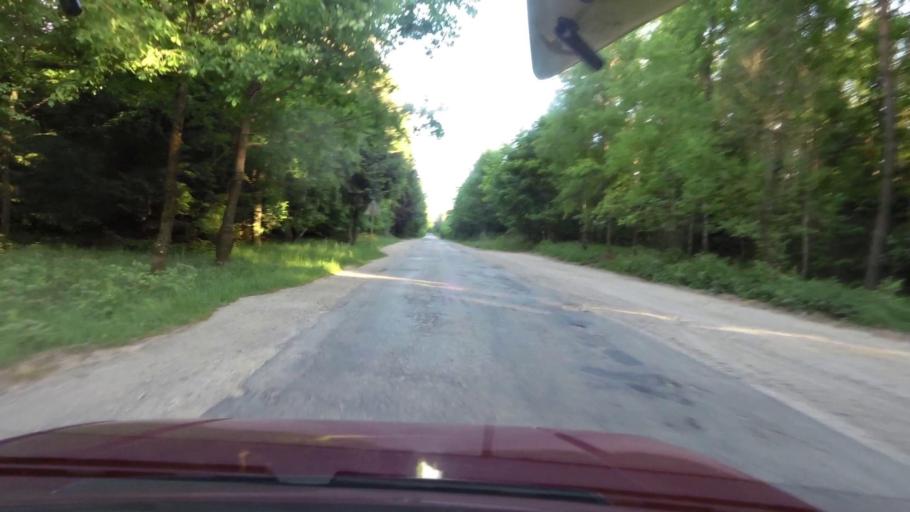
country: PL
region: West Pomeranian Voivodeship
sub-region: Powiat szczecinecki
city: Bialy Bor
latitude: 53.9312
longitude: 16.7995
